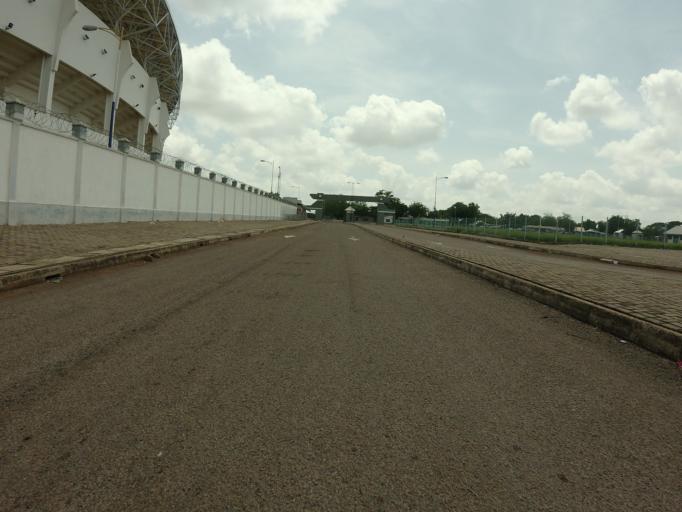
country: GH
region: Northern
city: Tamale
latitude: 9.4112
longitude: -0.8608
